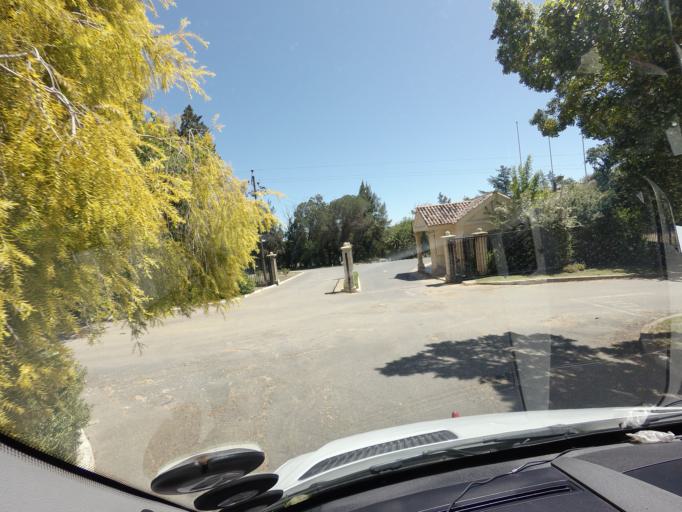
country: ZA
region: Western Cape
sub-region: Cape Winelands District Municipality
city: Stellenbosch
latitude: -33.8952
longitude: 18.8594
